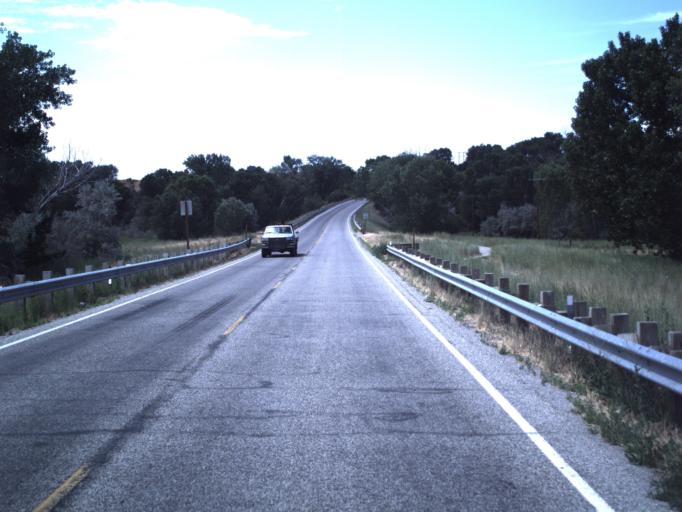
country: US
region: Utah
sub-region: Box Elder County
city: Elwood
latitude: 41.7133
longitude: -112.1172
